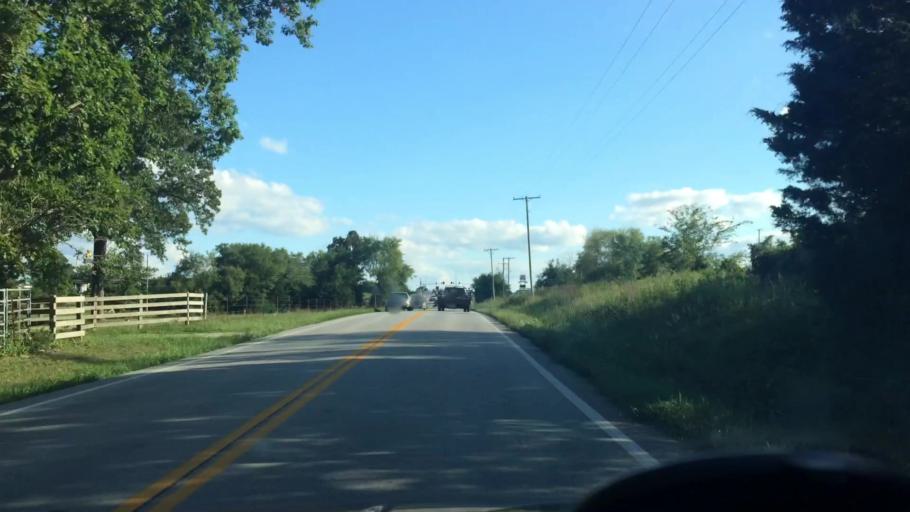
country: US
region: Missouri
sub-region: Greene County
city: Strafford
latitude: 37.2795
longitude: -93.1135
